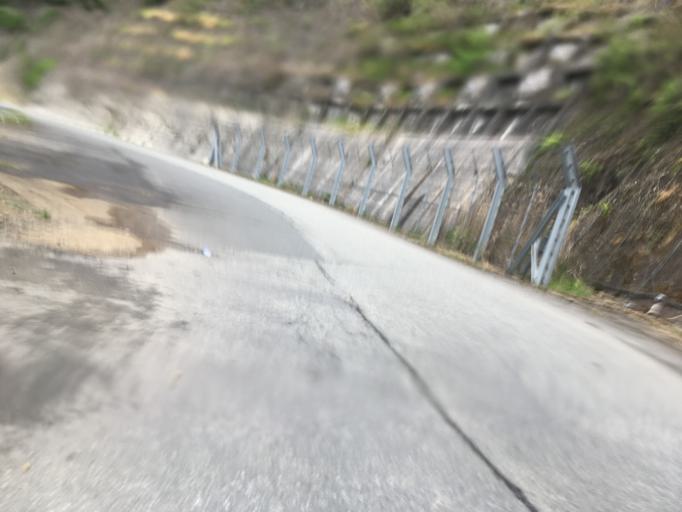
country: JP
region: Kyoto
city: Kameoka
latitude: 35.1429
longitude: 135.5756
